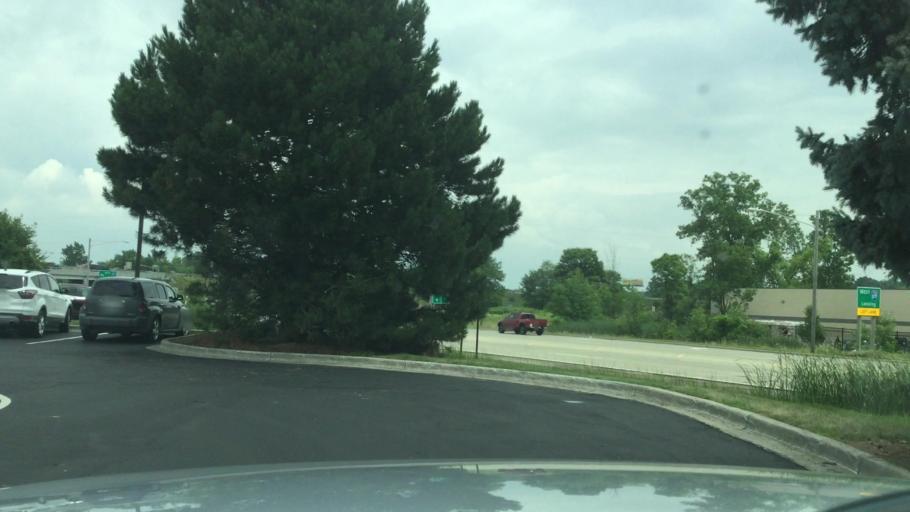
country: US
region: Michigan
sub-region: Genesee County
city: Swartz Creek
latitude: 42.9650
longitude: -83.8107
